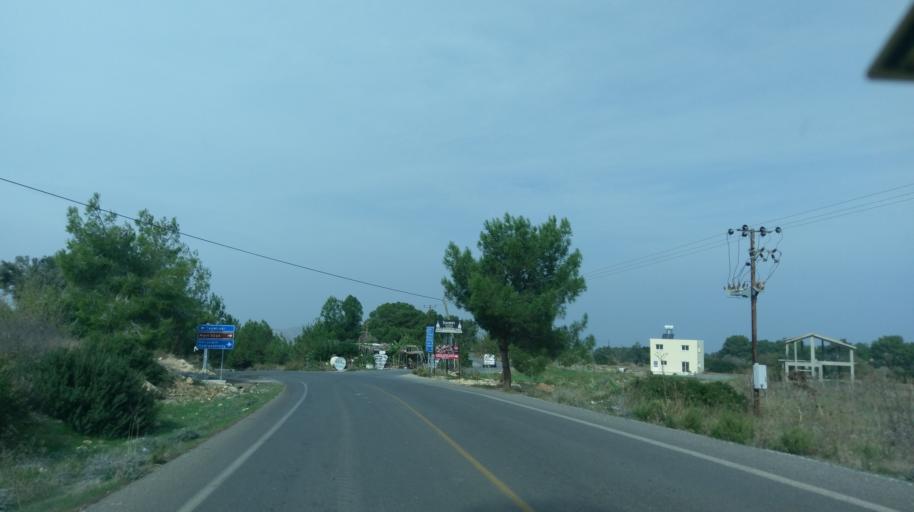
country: CY
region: Keryneia
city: Lapithos
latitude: 35.3125
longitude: 33.0577
